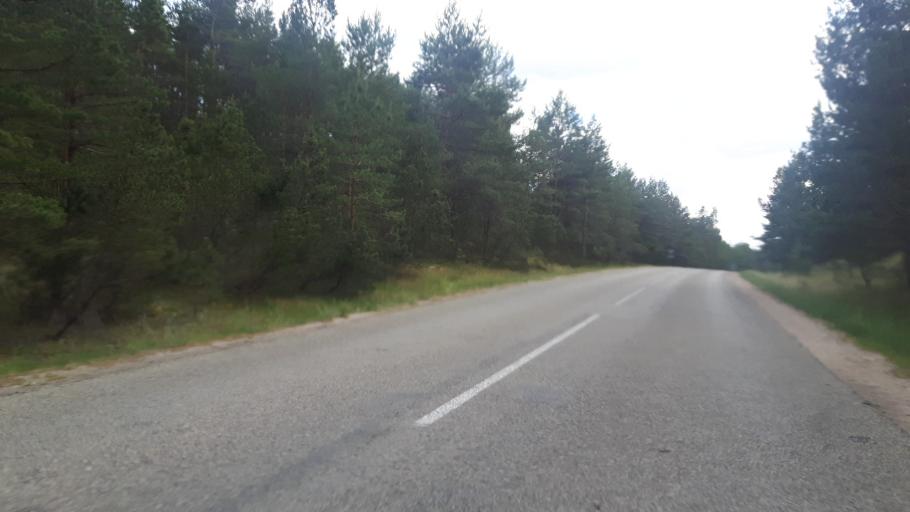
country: LV
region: Engure
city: Smarde
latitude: 57.0407
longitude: 23.3780
